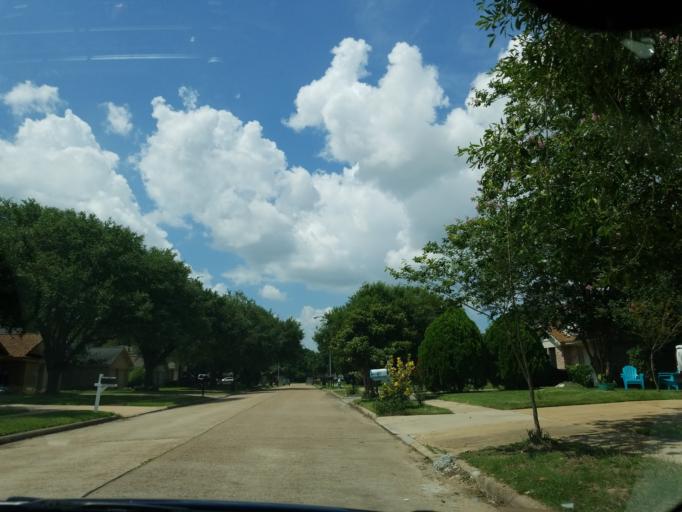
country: US
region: Texas
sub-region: Harris County
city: Cypress
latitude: 29.8743
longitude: -95.7294
